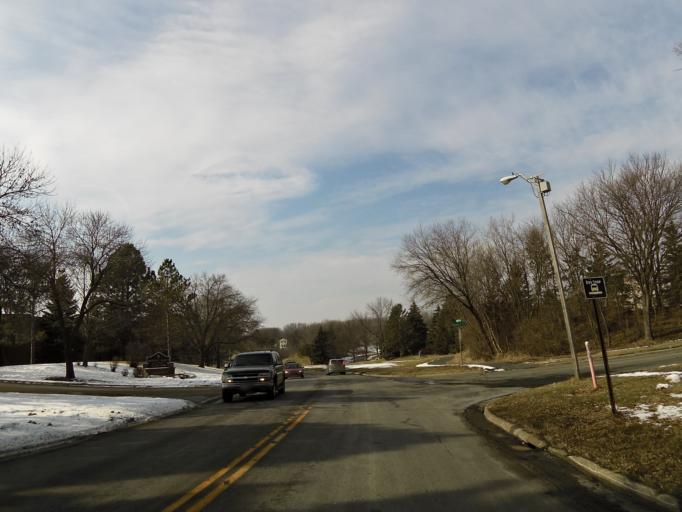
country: US
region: Minnesota
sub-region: Hennepin County
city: Eden Prairie
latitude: 44.8438
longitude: -93.4153
